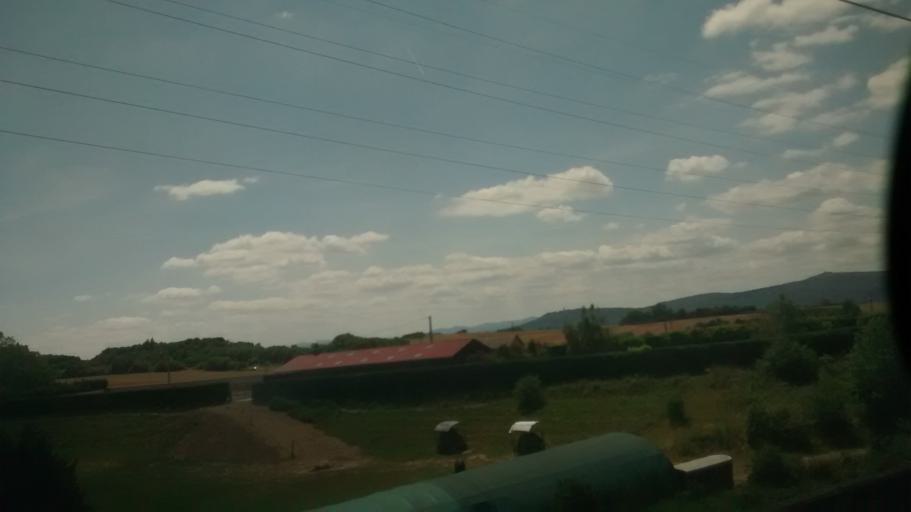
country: FR
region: Rhone-Alpes
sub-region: Departement du Rhone
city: Cailloux-sur-Fontaines
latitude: 45.8585
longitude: 4.9147
